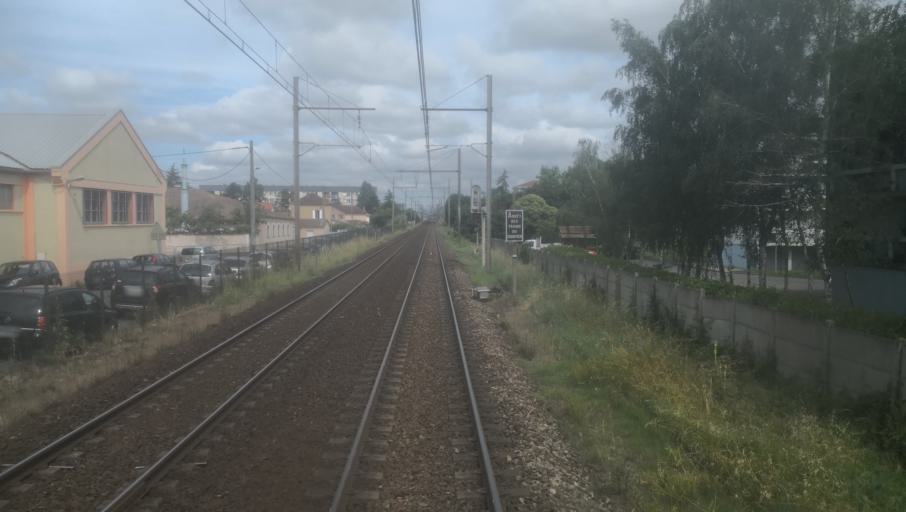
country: FR
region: Aquitaine
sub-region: Departement du Lot-et-Garonne
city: Marmande
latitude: 44.4981
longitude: 0.1768
